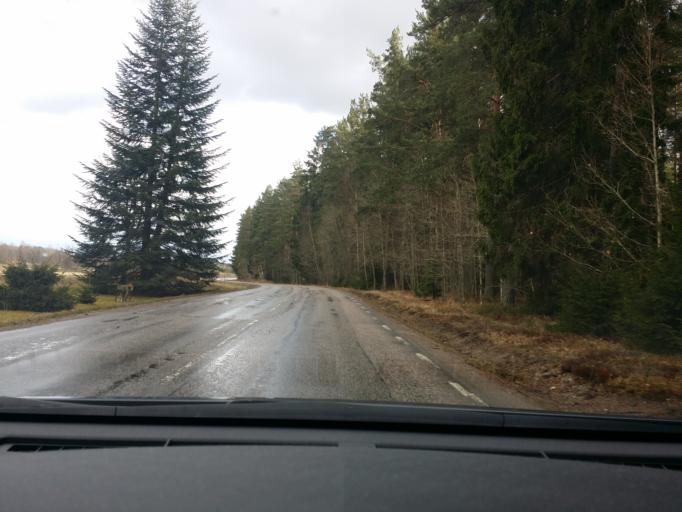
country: SE
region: Soedermanland
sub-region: Eskilstuna Kommun
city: Arla
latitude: 59.3119
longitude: 16.6805
